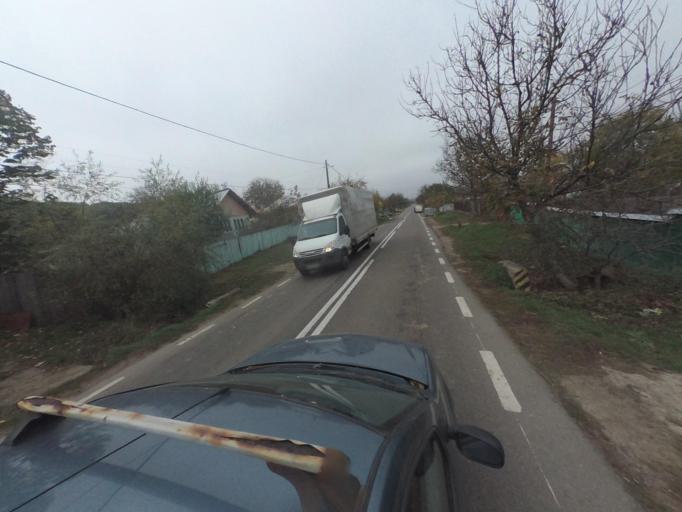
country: RO
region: Vaslui
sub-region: Comuna Bacesti
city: Bacesti
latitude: 46.8316
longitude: 27.2354
